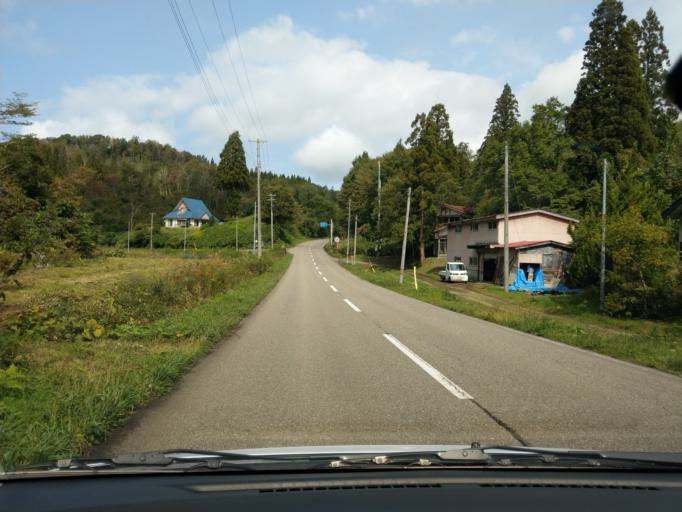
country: JP
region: Akita
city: Omagari
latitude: 39.4813
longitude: 140.3120
